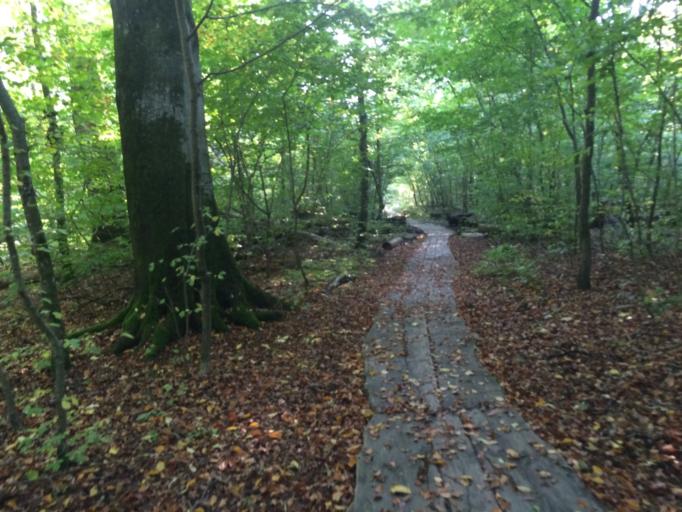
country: SE
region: Skane
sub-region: Lunds Kommun
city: Genarp
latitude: 55.6758
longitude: 13.3329
